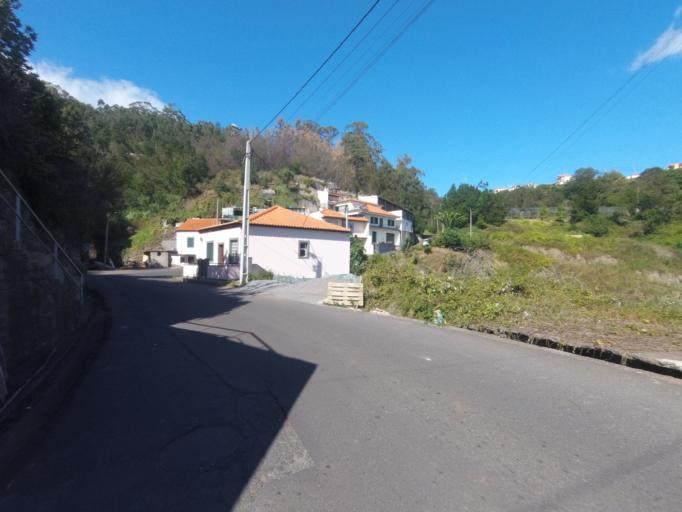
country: PT
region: Madeira
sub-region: Ribeira Brava
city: Campanario
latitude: 32.6803
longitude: -17.0284
